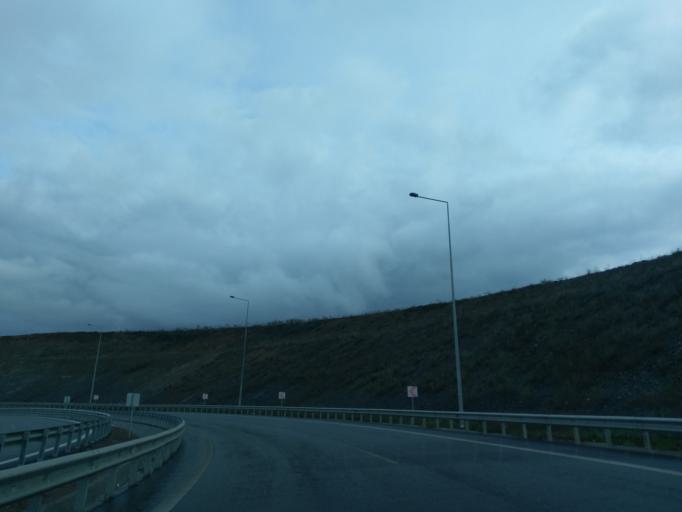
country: TR
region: Istanbul
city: Basaksehir
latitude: 41.0833
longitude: 28.8150
